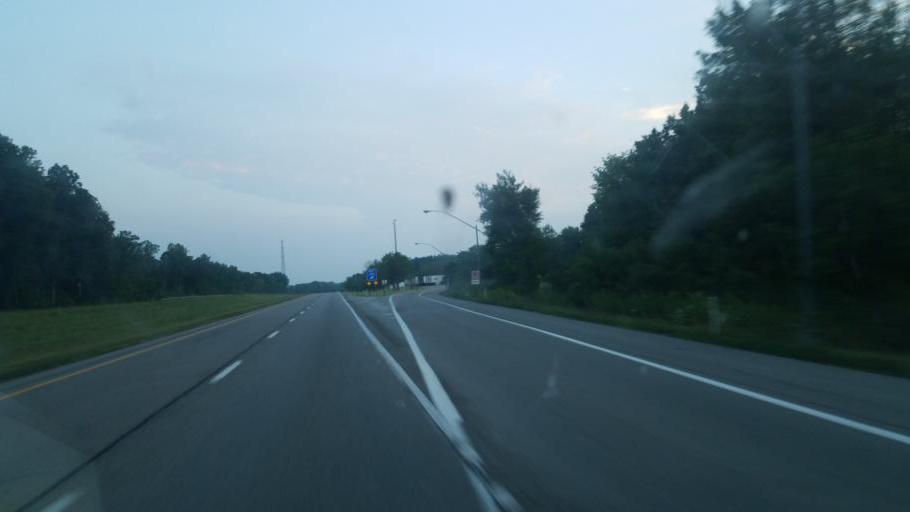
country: US
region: Pennsylvania
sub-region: Mercer County
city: Stoneboro
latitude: 41.4522
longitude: -80.1612
